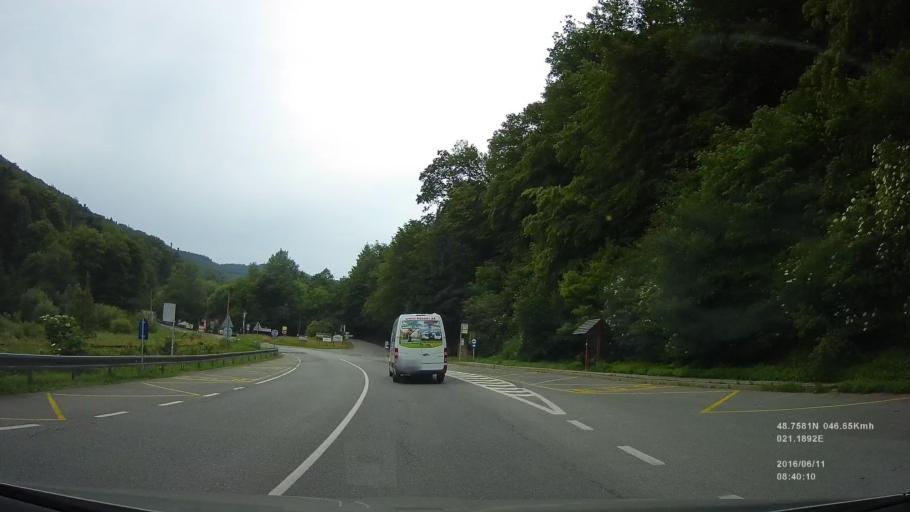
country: SK
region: Kosicky
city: Kosice
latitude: 48.7476
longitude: 21.2359
